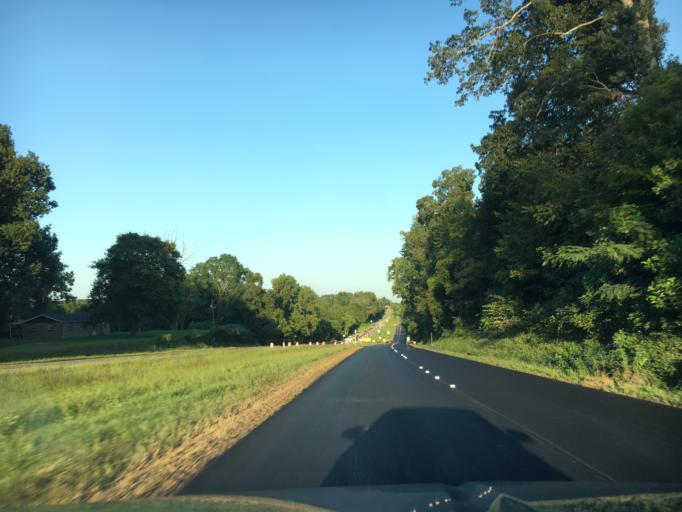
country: US
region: Virginia
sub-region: City of Danville
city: Danville
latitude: 36.5814
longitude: -79.2060
